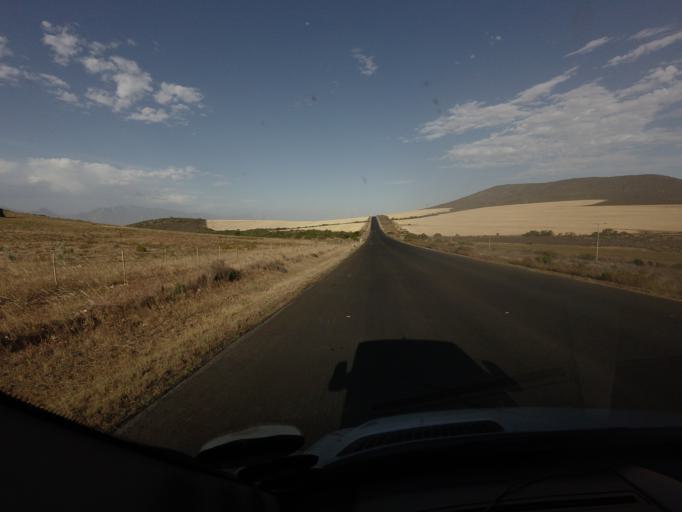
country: ZA
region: Western Cape
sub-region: Overberg District Municipality
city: Swellendam
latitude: -34.1058
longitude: 20.2469
